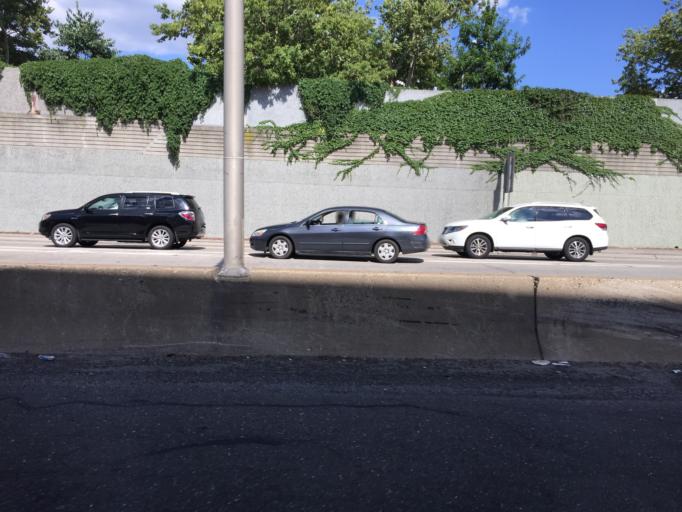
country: US
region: New York
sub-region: Queens County
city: Jamaica
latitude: 40.6717
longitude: -73.8011
